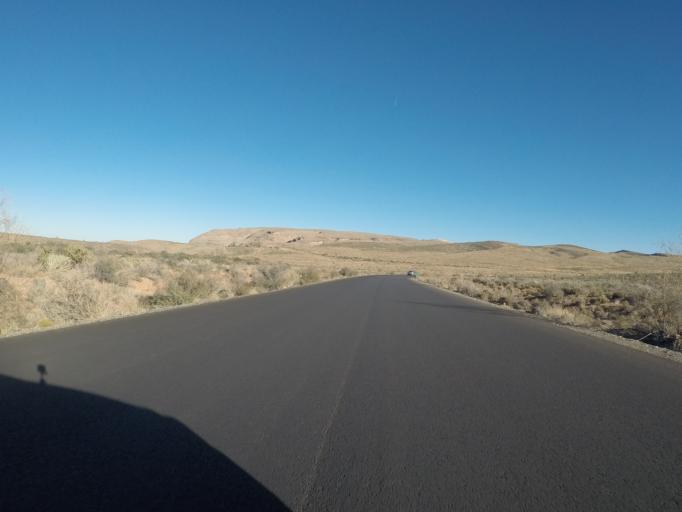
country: US
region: Nevada
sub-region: Clark County
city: Summerlin South
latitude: 36.1160
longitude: -115.4538
